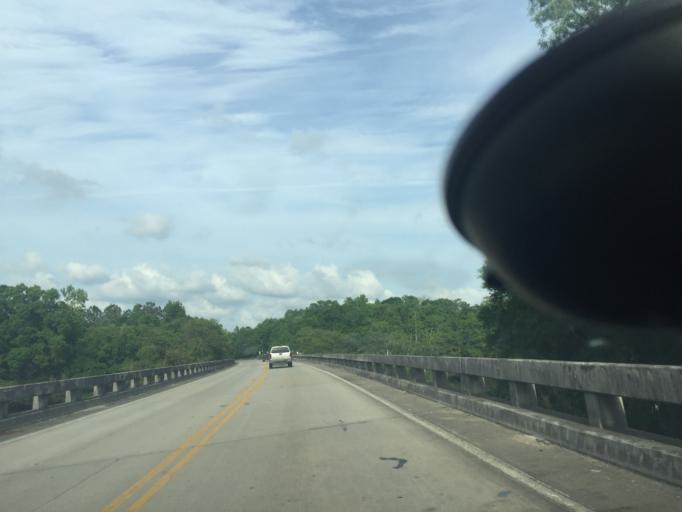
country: US
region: Georgia
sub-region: Chatham County
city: Bloomingdale
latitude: 32.0795
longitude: -81.3856
